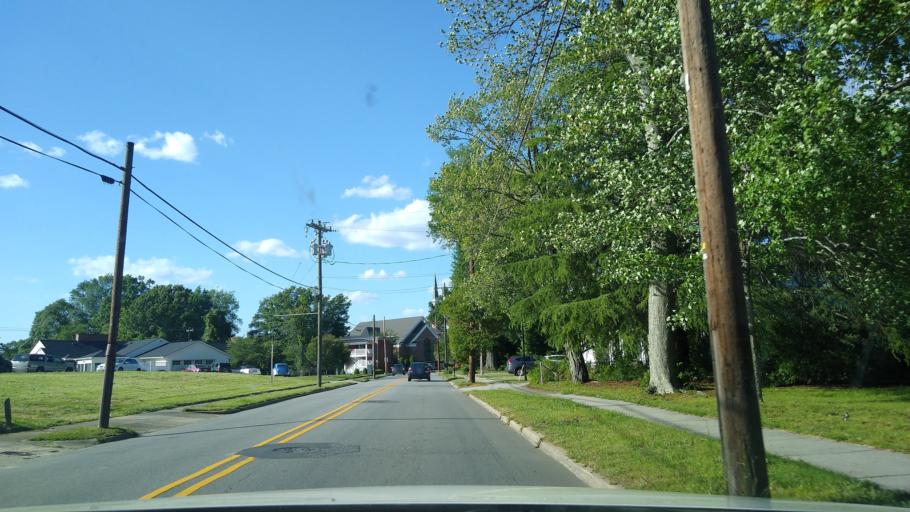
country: US
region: North Carolina
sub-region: Forsyth County
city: Kernersville
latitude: 36.1151
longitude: -80.0773
